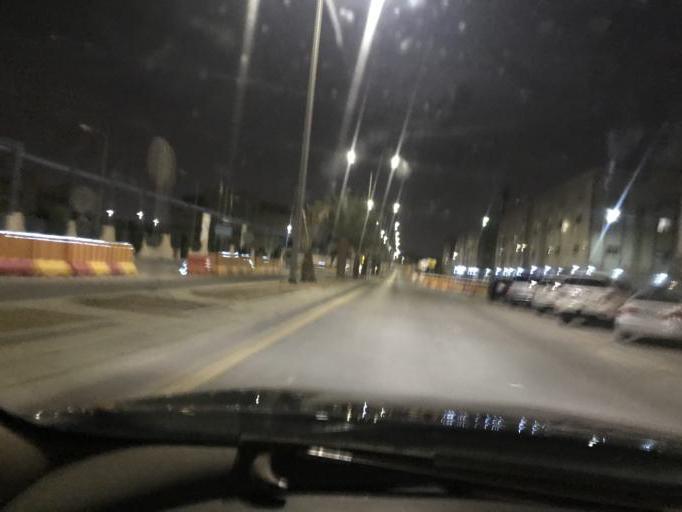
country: SA
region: Ar Riyad
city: Riyadh
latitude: 24.8003
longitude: 46.7079
